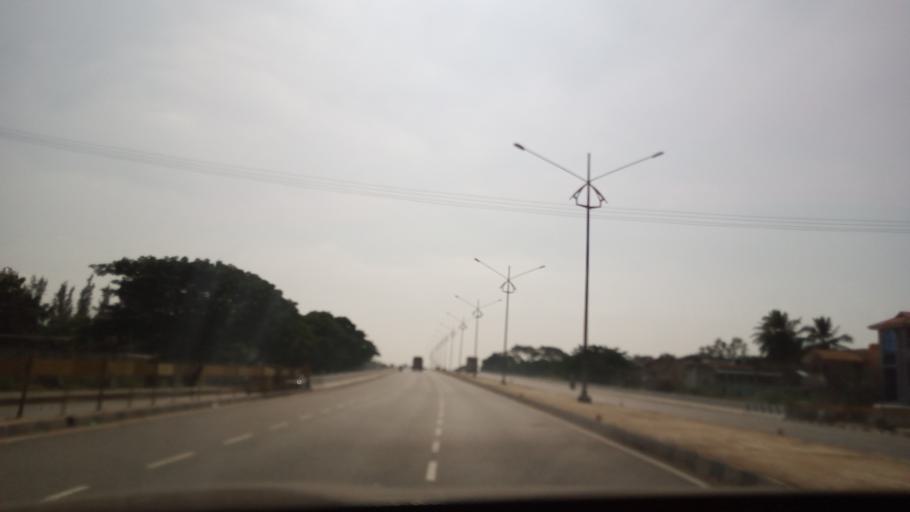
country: IN
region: Tamil Nadu
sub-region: Vellore
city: Vaniyambadi
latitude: 12.6796
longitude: 78.6247
